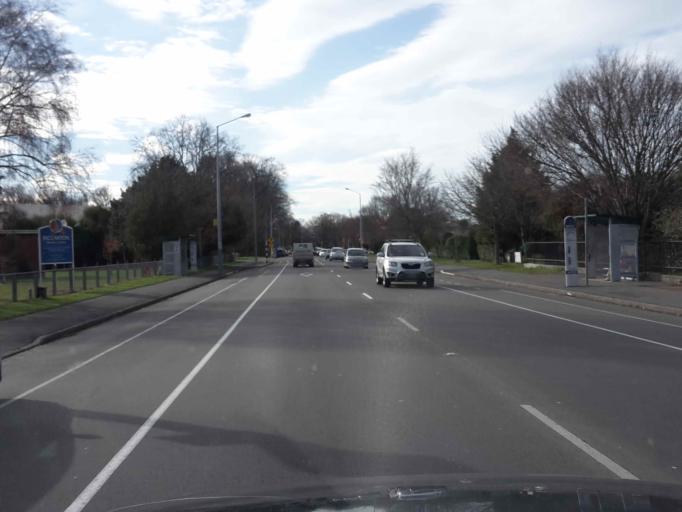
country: NZ
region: Canterbury
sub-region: Selwyn District
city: Prebbleton
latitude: -43.5341
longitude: 172.5636
